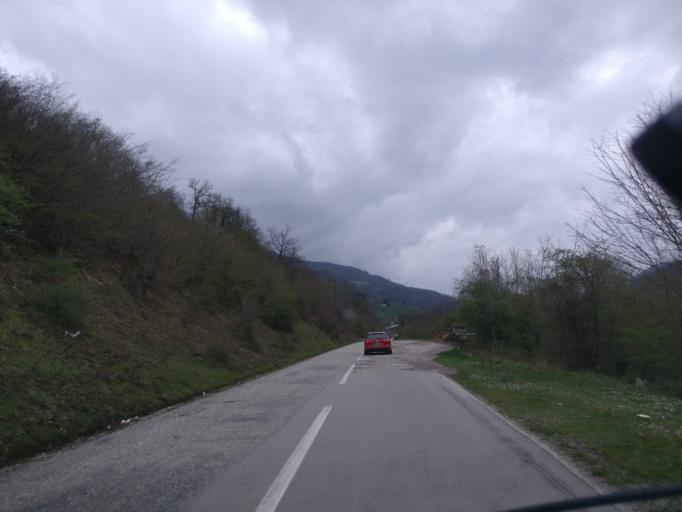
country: BA
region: Republika Srpska
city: Foca
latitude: 43.4437
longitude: 18.7582
